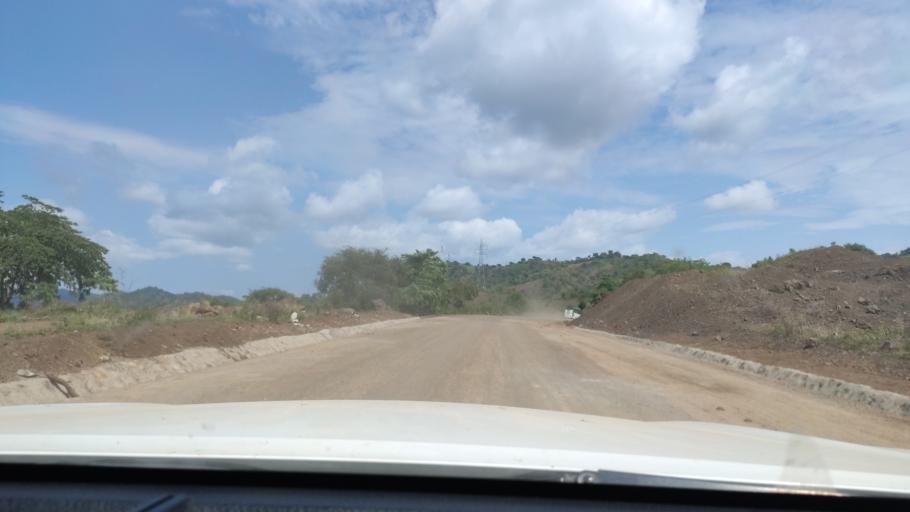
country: ET
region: Southern Nations, Nationalities, and People's Region
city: Felege Neway
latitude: 6.3914
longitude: 37.0595
